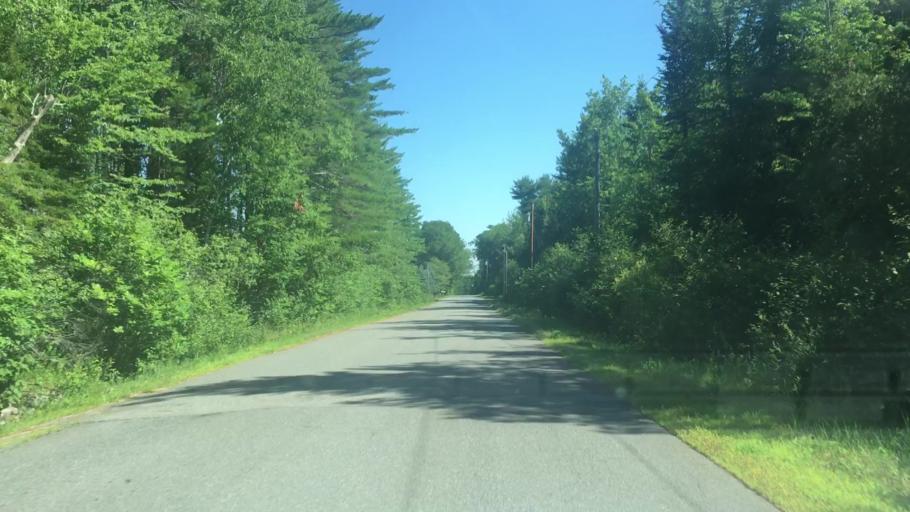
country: US
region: Maine
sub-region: Waldo County
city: Northport
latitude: 44.3768
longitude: -68.9825
